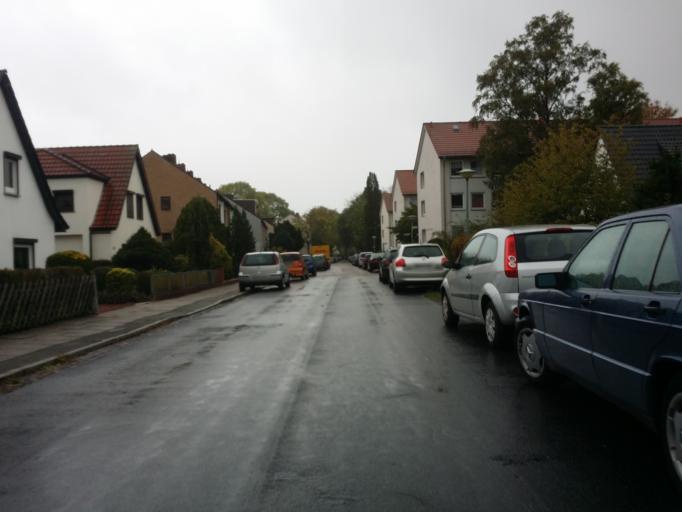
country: DE
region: Bremen
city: Bremen
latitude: 53.0324
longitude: 8.8163
